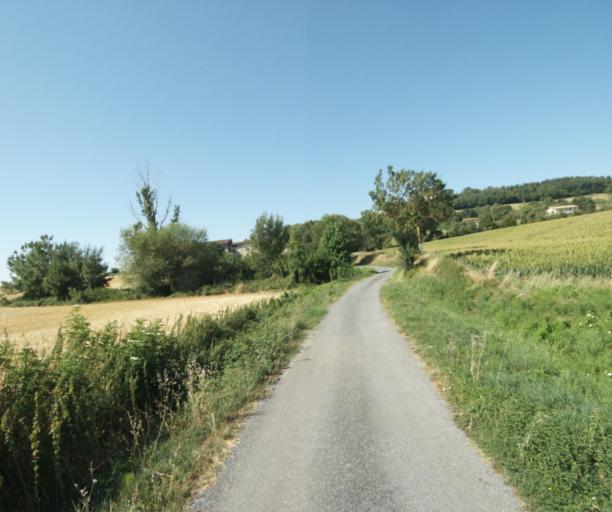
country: FR
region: Midi-Pyrenees
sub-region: Departement de la Haute-Garonne
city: Saint-Felix-Lauragais
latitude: 43.5152
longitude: 1.9396
